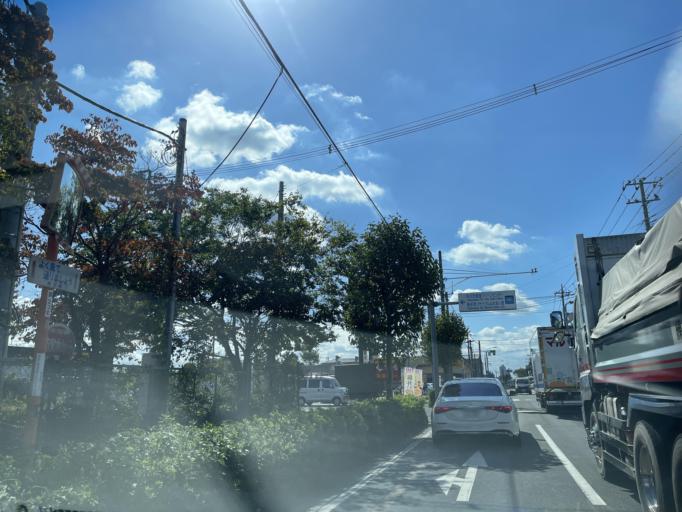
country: JP
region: Saitama
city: Tokorozawa
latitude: 35.8092
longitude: 139.4935
